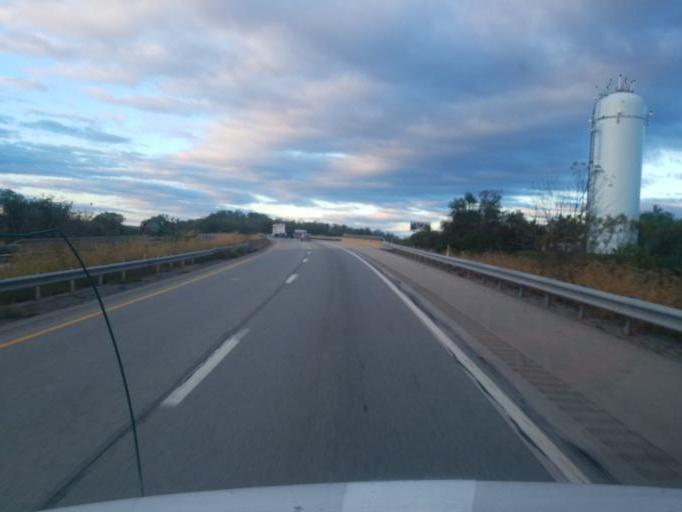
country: US
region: Pennsylvania
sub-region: York County
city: Shiloh
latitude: 39.9586
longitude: -76.7847
